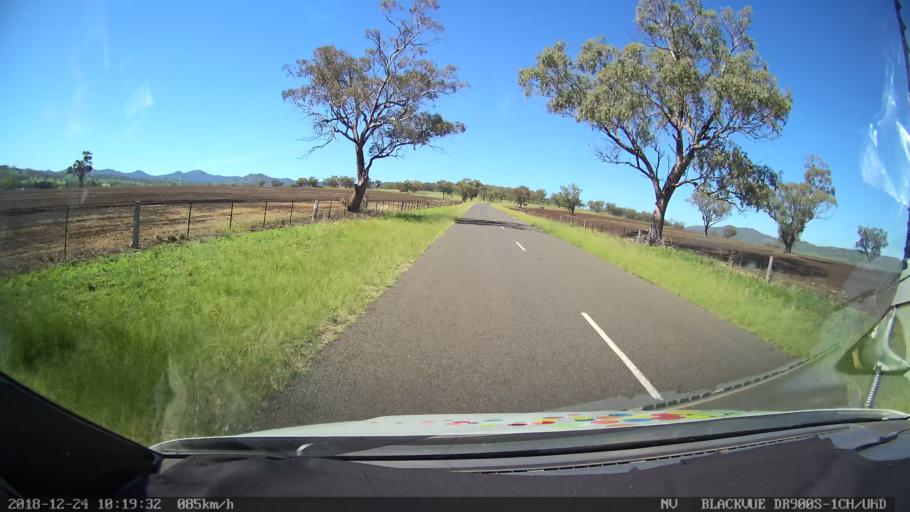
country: AU
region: New South Wales
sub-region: Liverpool Plains
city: Quirindi
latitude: -31.7317
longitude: 150.5650
